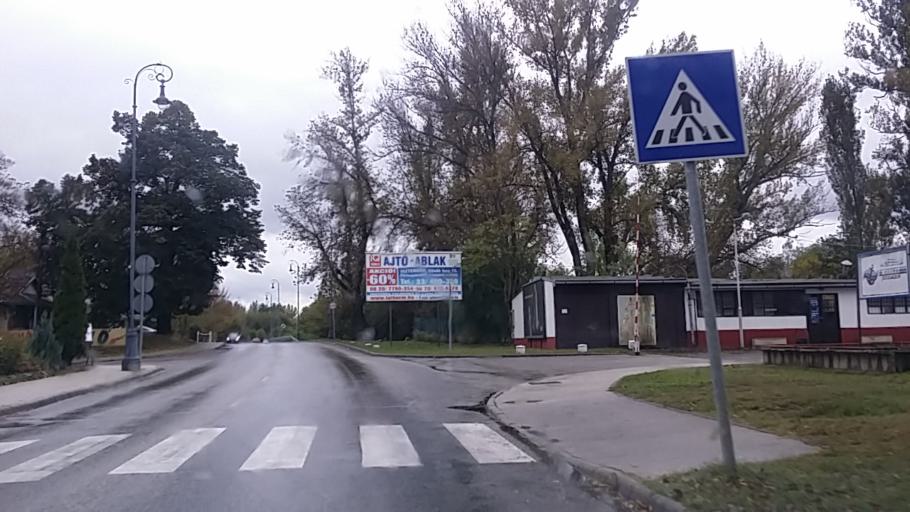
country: HU
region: Komarom-Esztergom
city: Esztergom
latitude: 47.7930
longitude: 18.7325
